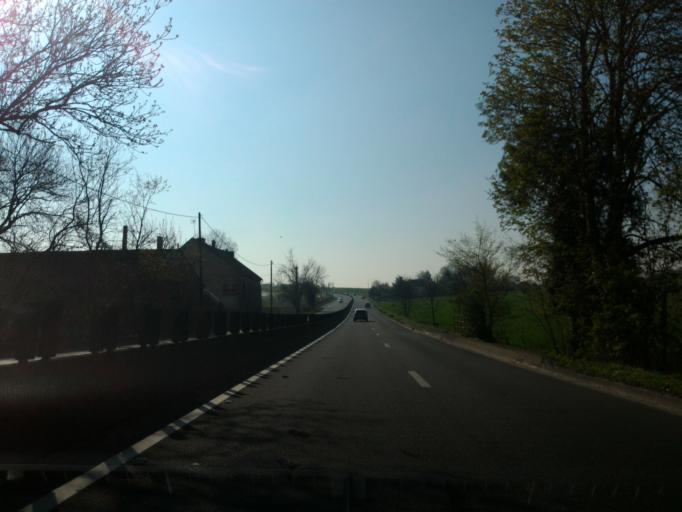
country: FR
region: Ile-de-France
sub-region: Departement du Val-de-Marne
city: Ormesson-sur-Marne
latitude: 48.7881
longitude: 2.5620
